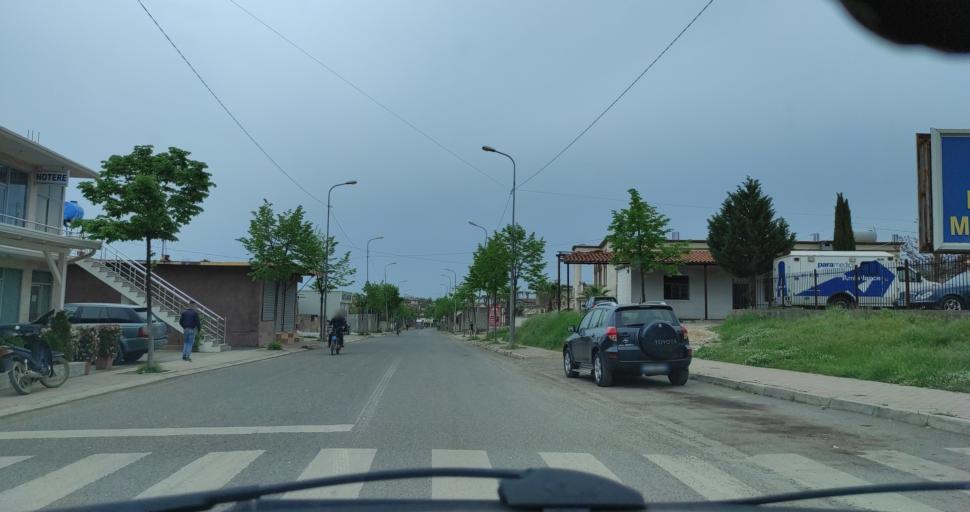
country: AL
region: Lezhe
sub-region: Rrethi i Kurbinit
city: Mamurras
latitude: 41.5799
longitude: 19.6921
